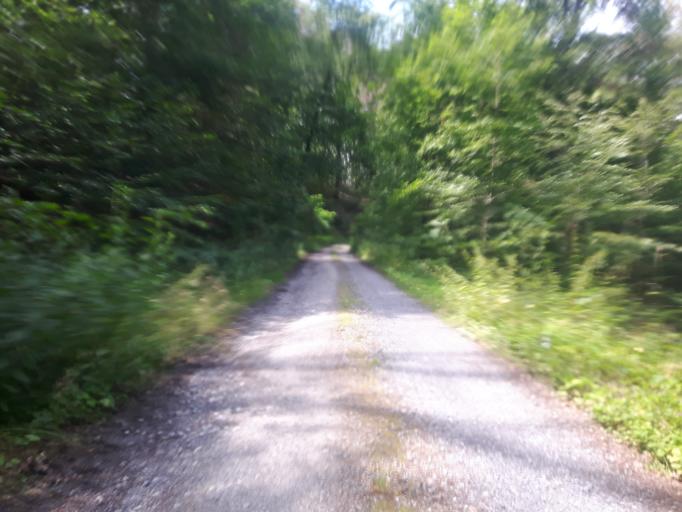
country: DE
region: Baden-Wuerttemberg
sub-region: Regierungsbezirk Stuttgart
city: Pfaffenhofen
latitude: 49.0432
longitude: 8.9584
